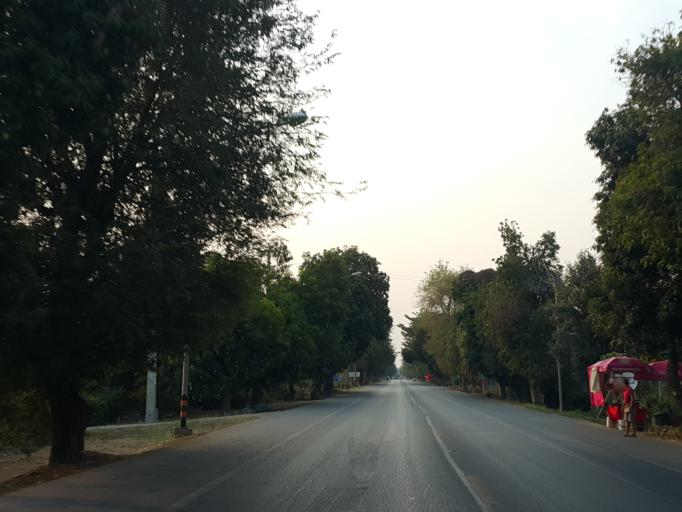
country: TH
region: Sukhothai
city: Si Samrong
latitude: 17.2159
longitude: 99.8644
